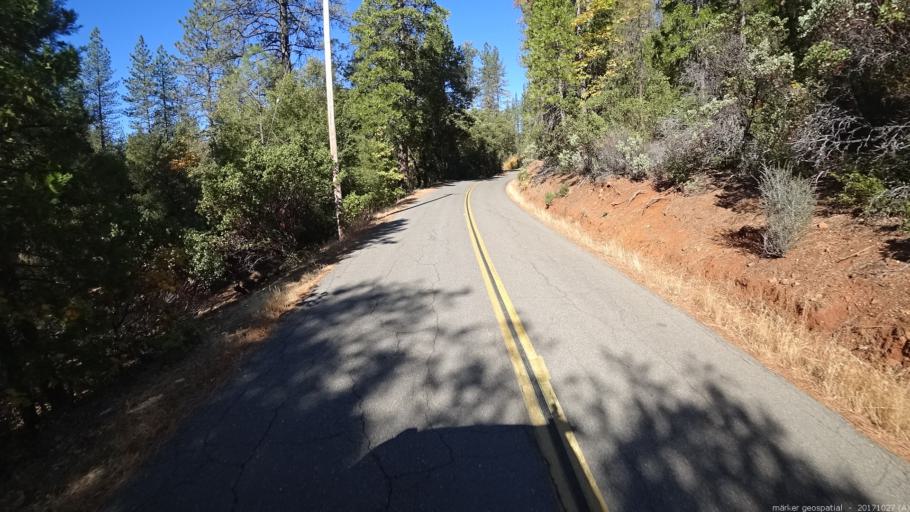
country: US
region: California
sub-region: Shasta County
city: Shingletown
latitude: 40.7500
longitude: -121.9488
